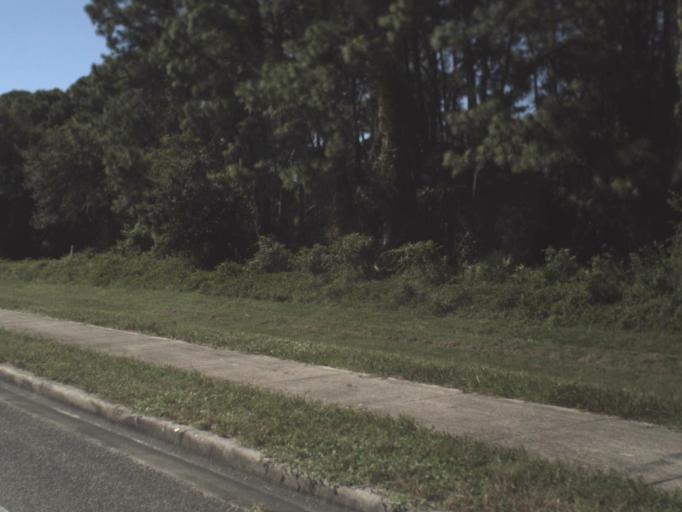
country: US
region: Florida
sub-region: Sarasota County
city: North Port
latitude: 27.0047
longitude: -82.1705
